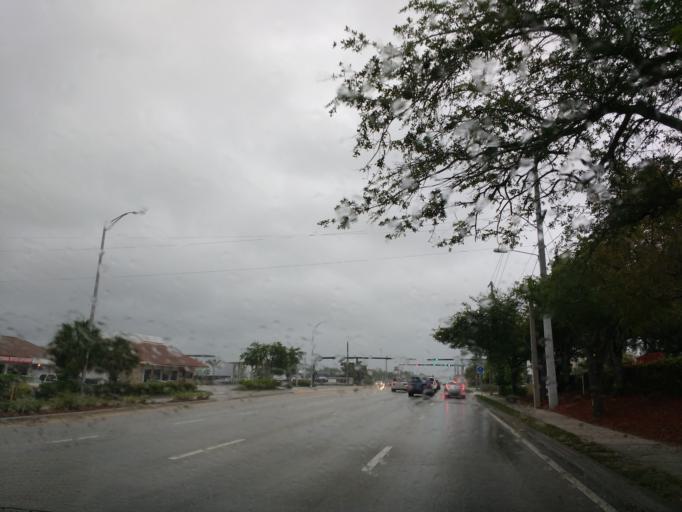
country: US
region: Florida
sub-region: Collier County
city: Naples
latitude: 26.1373
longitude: -81.7664
